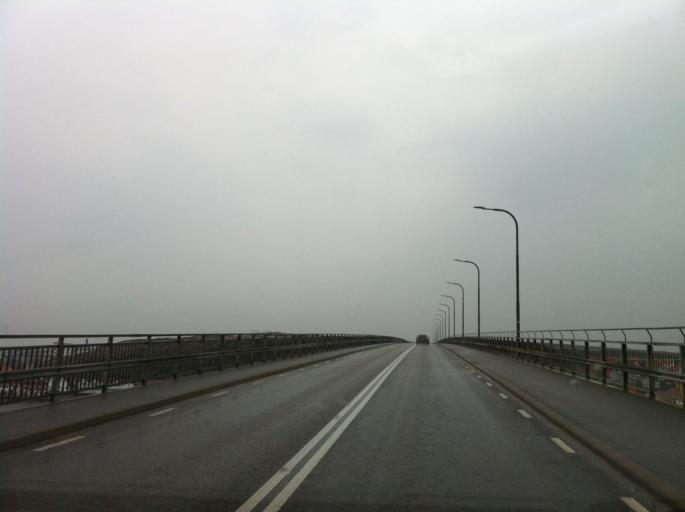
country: SE
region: Vaestra Goetaland
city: Smoegen
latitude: 58.3641
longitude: 11.2394
